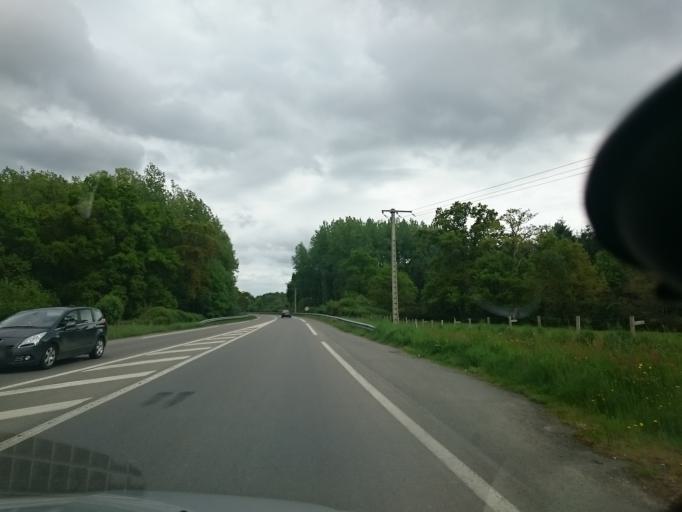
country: FR
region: Brittany
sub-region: Departement d'Ille-et-Vilaine
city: Saint-Brice-en-Cogles
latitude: 48.3986
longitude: -1.3717
